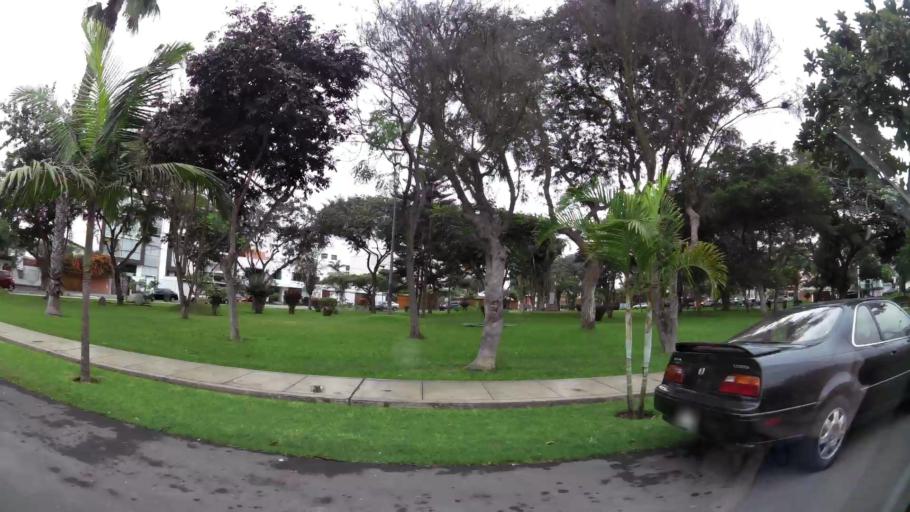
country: PE
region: Lima
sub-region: Lima
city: Surco
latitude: -12.1234
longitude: -77.0099
